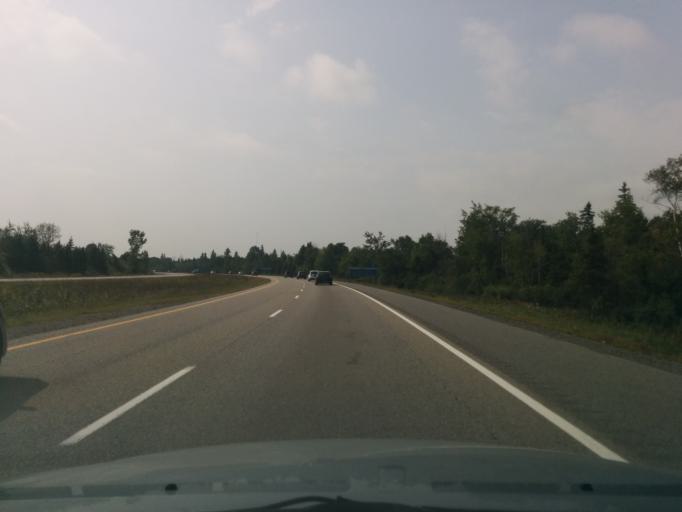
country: CA
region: Ontario
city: Bells Corners
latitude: 45.2891
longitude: -75.8039
